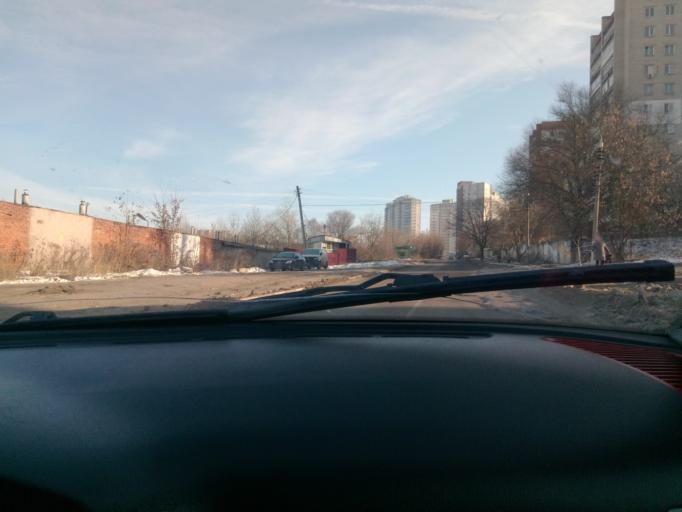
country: RU
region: Tula
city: Mendeleyevskiy
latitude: 54.1680
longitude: 37.5621
